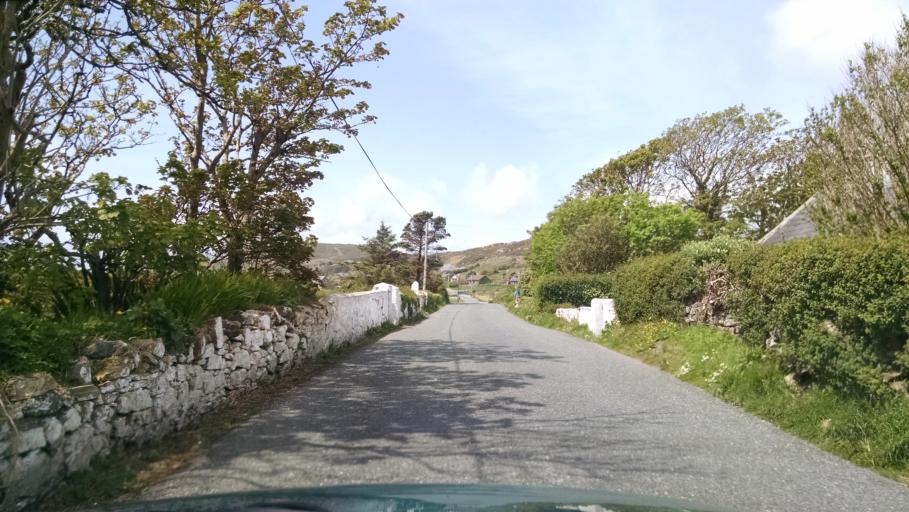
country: IE
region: Connaught
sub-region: County Galway
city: Clifden
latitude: 53.4906
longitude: -10.0450
